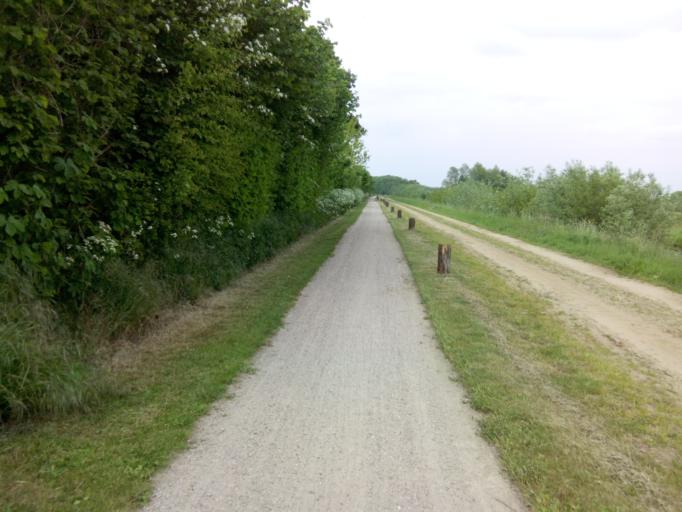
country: NL
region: Gelderland
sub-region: Berkelland
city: Borculo
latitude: 52.0559
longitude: 6.5250
